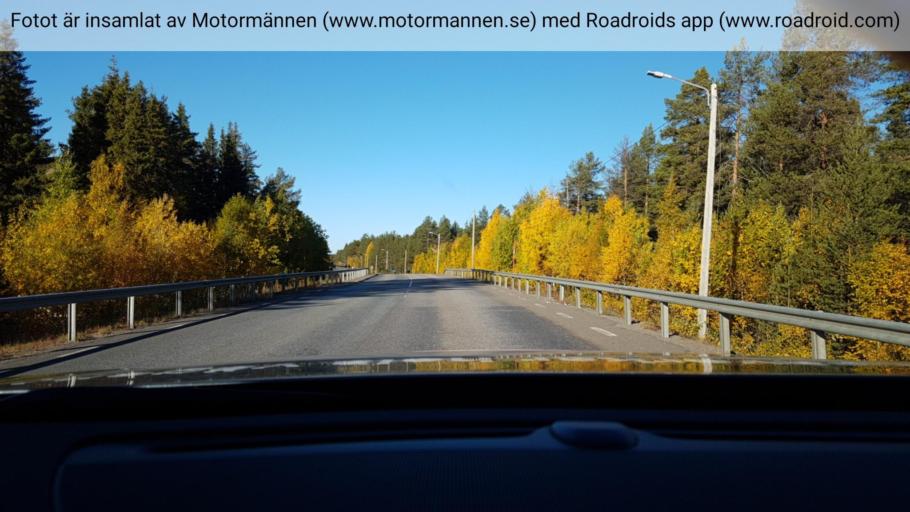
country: SE
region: Vaesterbotten
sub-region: Skelleftea Kommun
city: Storvik
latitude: 65.3847
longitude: 20.3360
